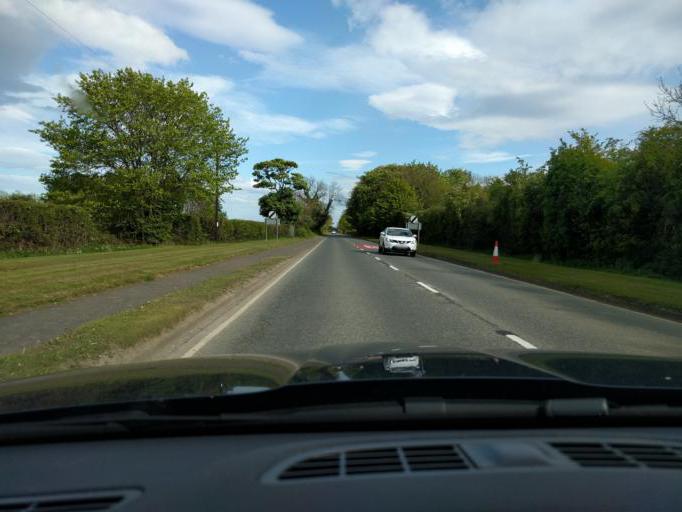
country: GB
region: England
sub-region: Northumberland
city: Morpeth
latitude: 55.1548
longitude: -1.6723
